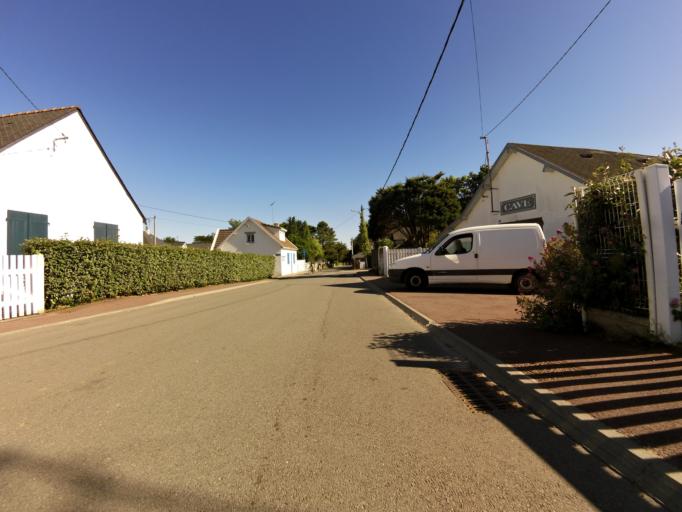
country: FR
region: Brittany
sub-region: Departement du Morbihan
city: Penestin
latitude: 47.4741
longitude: -2.4843
